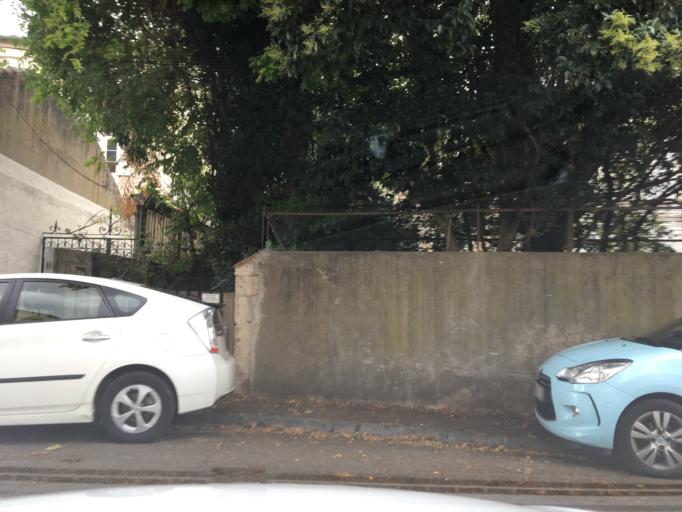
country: FR
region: Aquitaine
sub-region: Departement du Lot-et-Garonne
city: Le Passage
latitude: 44.2035
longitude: 0.6137
